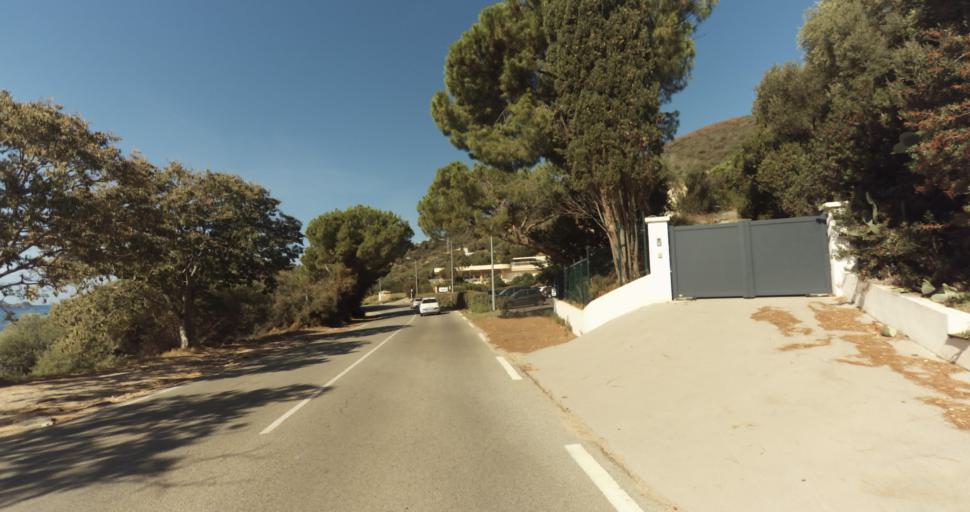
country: FR
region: Corsica
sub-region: Departement de la Corse-du-Sud
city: Ajaccio
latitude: 41.9079
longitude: 8.6336
